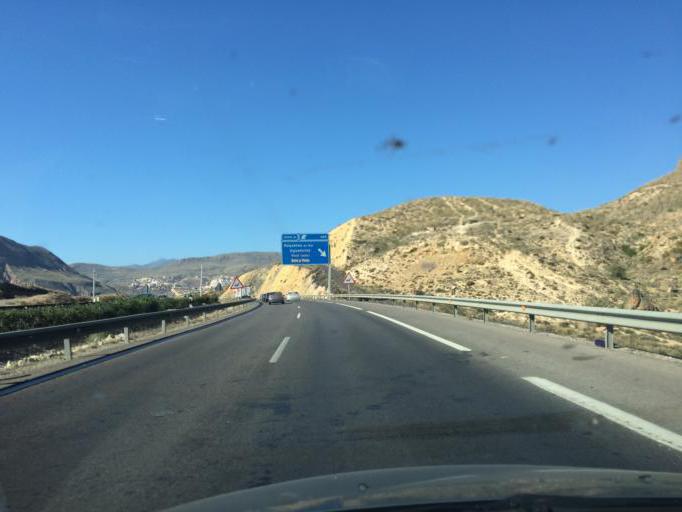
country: ES
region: Andalusia
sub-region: Provincia de Almeria
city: Aguadulce
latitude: 36.8268
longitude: -2.5828
